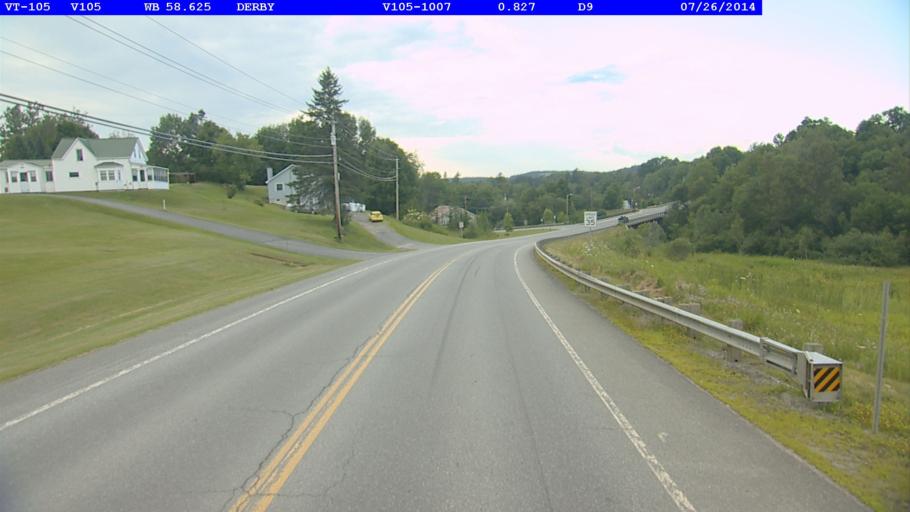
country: US
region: Vermont
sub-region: Orleans County
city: Newport
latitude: 44.9433
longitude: -72.1334
